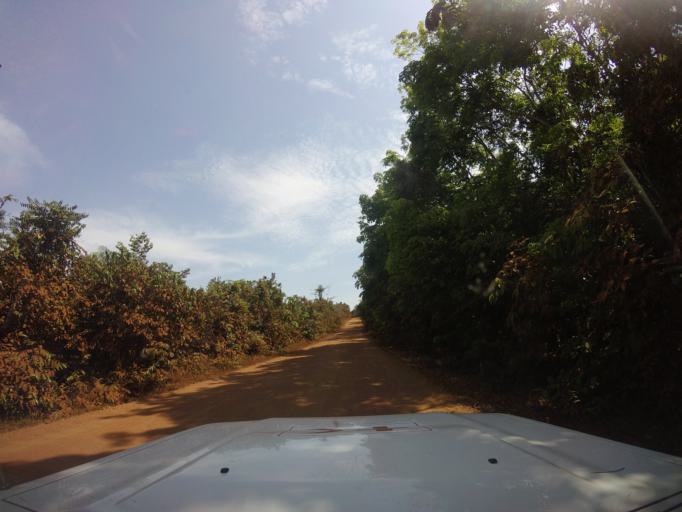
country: LR
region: Grand Cape Mount
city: Robertsport
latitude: 6.7203
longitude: -11.3364
